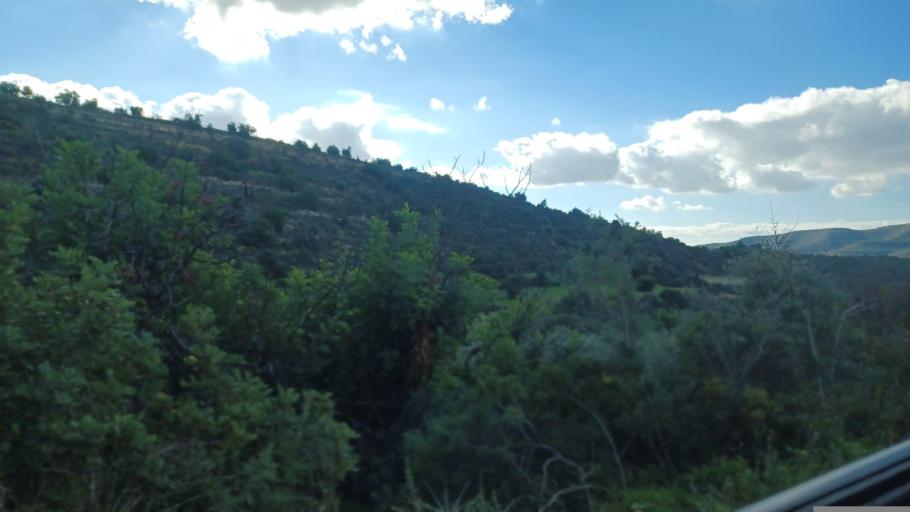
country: CY
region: Limassol
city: Pano Polemidia
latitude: 34.7637
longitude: 32.9790
